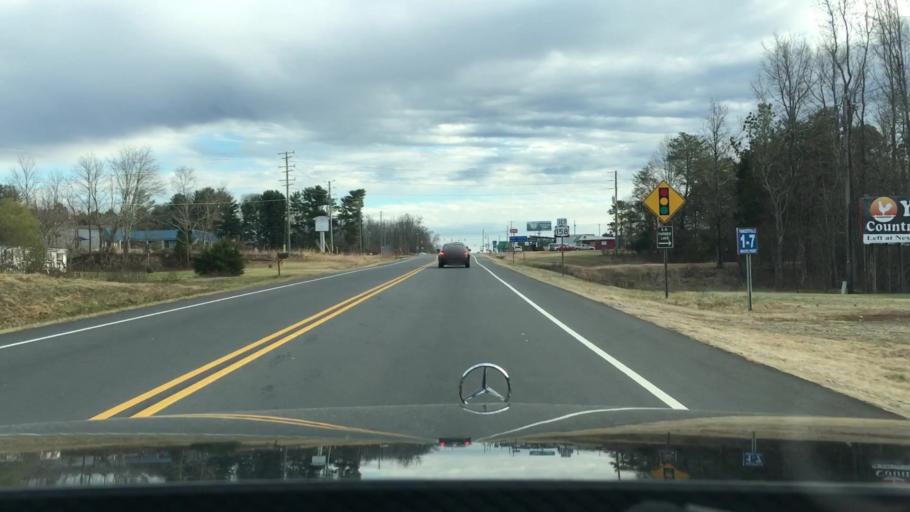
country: US
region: North Carolina
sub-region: Caswell County
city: Yanceyville
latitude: 36.4214
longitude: -79.3535
